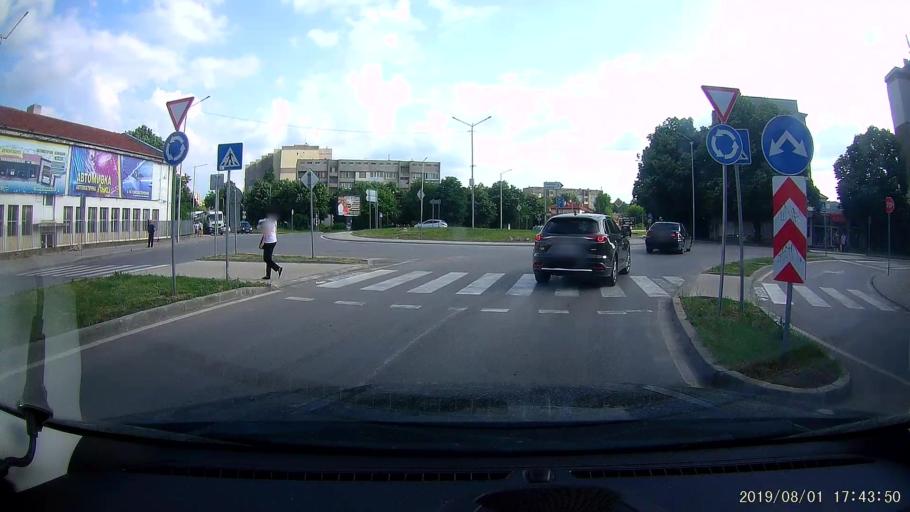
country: BG
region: Silistra
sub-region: Obshtina Silistra
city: Silistra
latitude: 44.1124
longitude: 27.2724
